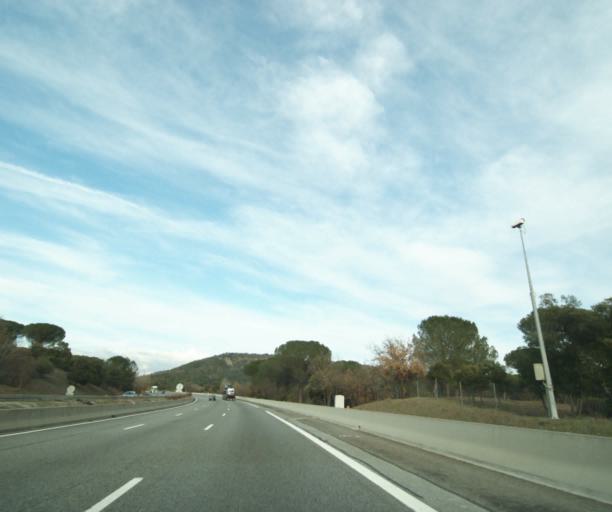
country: FR
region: Provence-Alpes-Cote d'Azur
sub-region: Departement du Var
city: Vidauban
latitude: 43.4214
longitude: 6.4677
